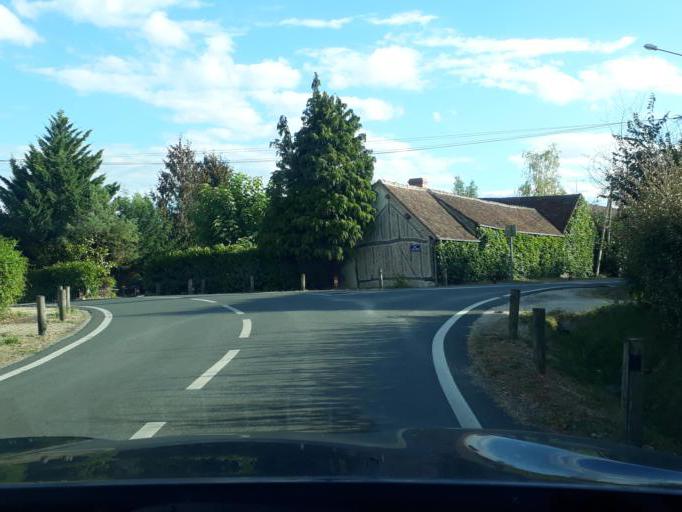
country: FR
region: Centre
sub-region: Departement du Loiret
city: Rebrechien
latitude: 47.9856
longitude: 2.0342
